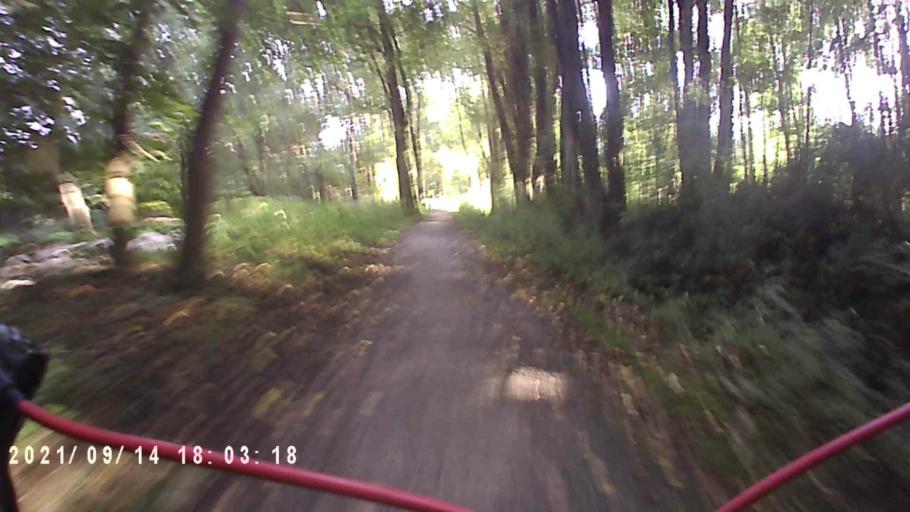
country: NL
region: Drenthe
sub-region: Gemeente Tynaarlo
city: Zuidlaren
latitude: 53.1140
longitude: 6.6524
